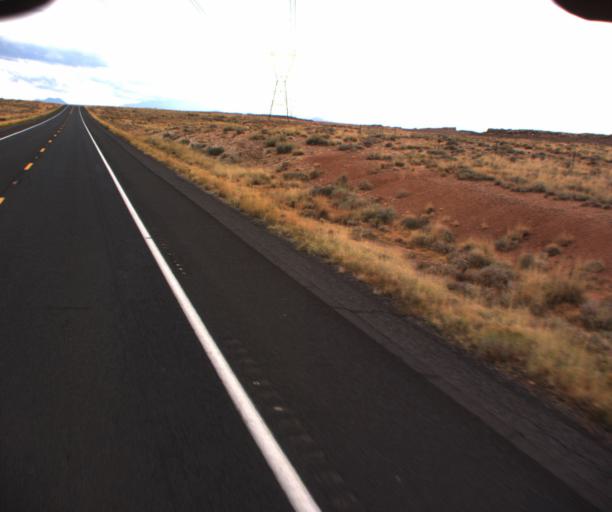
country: US
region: Arizona
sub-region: Coconino County
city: Tuba City
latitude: 35.8184
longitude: -111.4414
